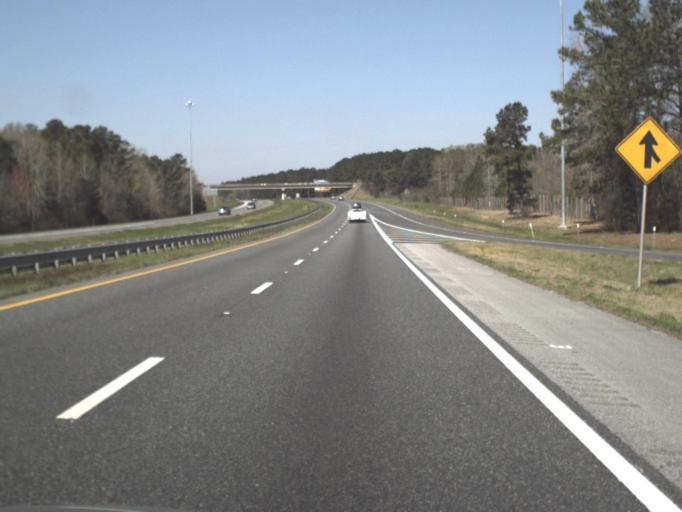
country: US
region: Florida
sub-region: Jackson County
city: Marianna
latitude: 30.7549
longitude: -85.2759
